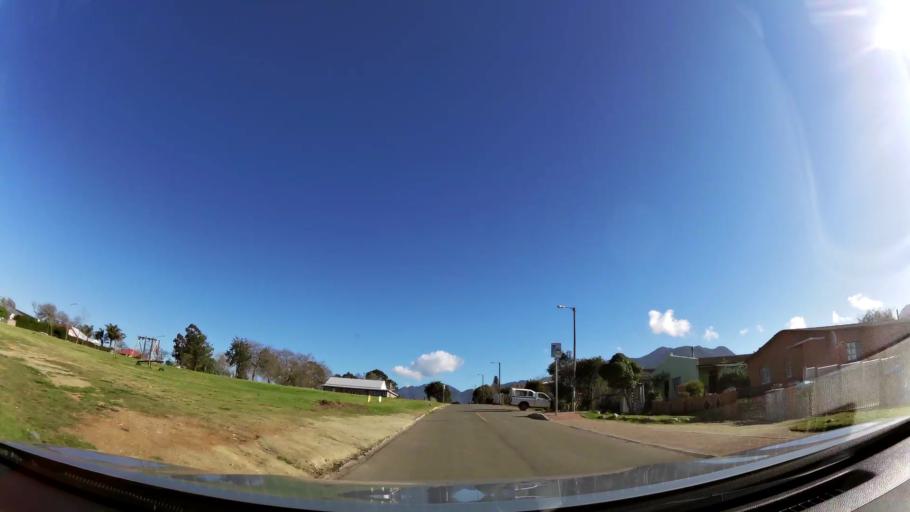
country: ZA
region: Western Cape
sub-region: Eden District Municipality
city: George
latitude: -33.9482
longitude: 22.4223
